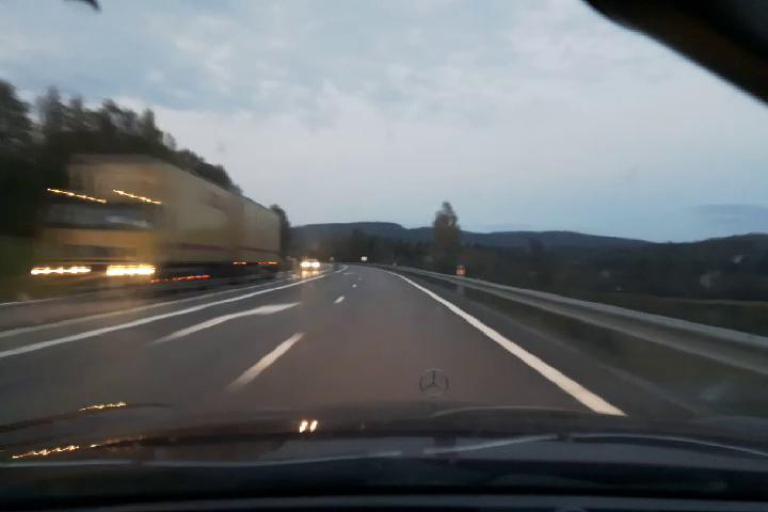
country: SE
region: Vaesternorrland
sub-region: Kramfors Kommun
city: Nordingra
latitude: 62.9655
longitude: 18.1550
